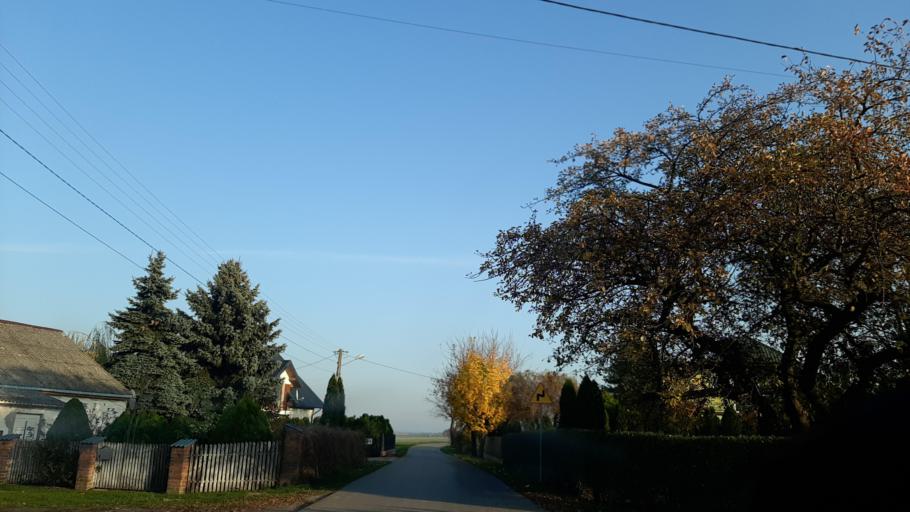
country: PL
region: Lublin Voivodeship
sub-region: Powiat lubelski
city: Garbow
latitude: 51.3837
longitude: 22.3422
